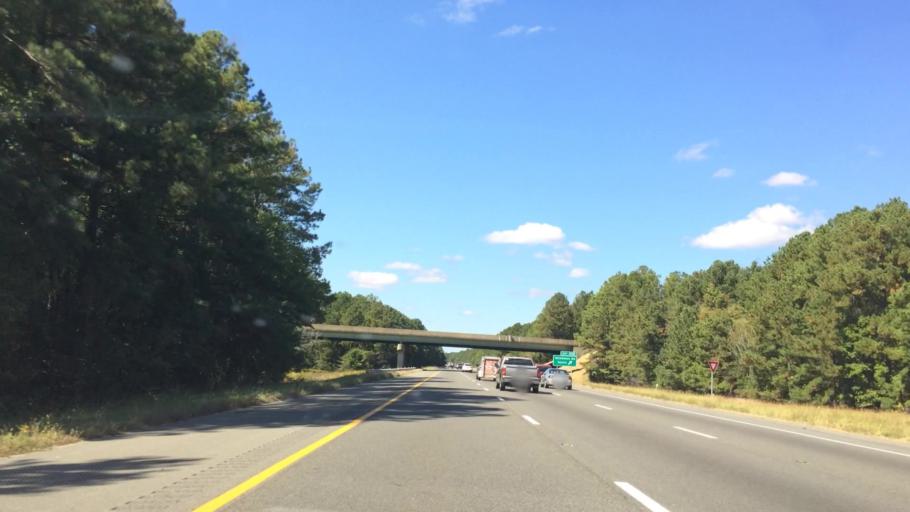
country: US
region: Virginia
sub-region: Henrico County
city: Glen Allen
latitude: 37.6665
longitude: -77.4829
